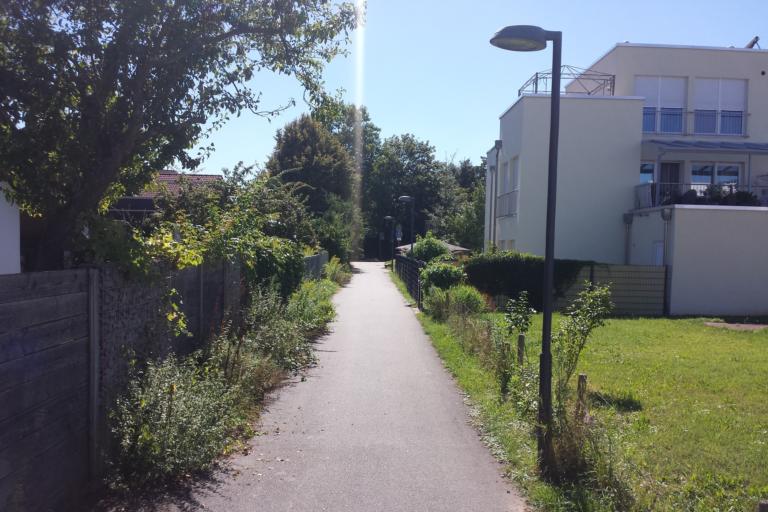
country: DE
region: Baden-Wuerttemberg
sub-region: Karlsruhe Region
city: Eppelheim
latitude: 49.3813
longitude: 8.6578
